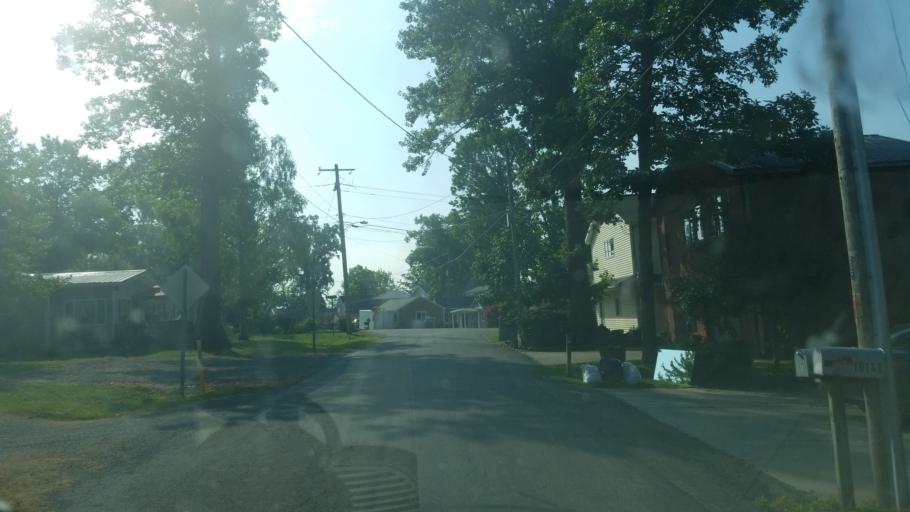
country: US
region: Ohio
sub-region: Logan County
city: Russells Point
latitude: 40.4951
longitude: -83.8747
